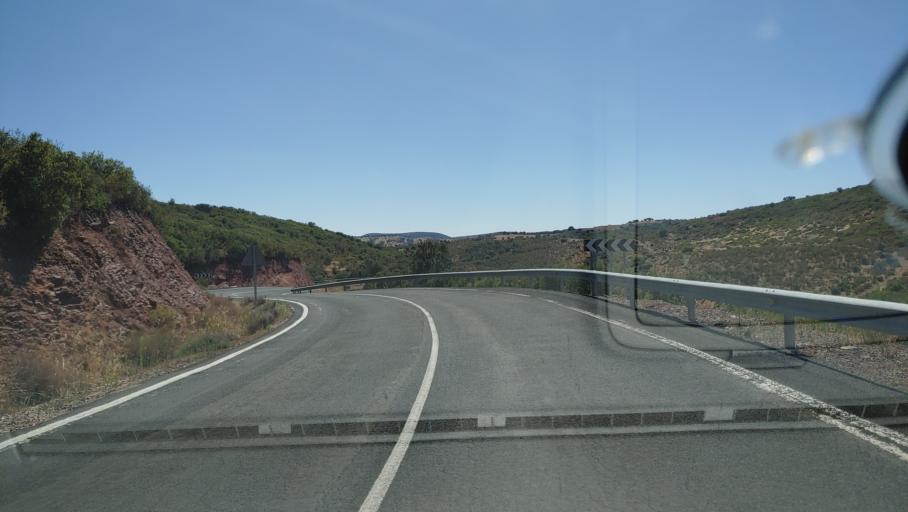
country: ES
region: Castille-La Mancha
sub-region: Provincia de Ciudad Real
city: Albaladejo
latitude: 38.5213
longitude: -2.7844
